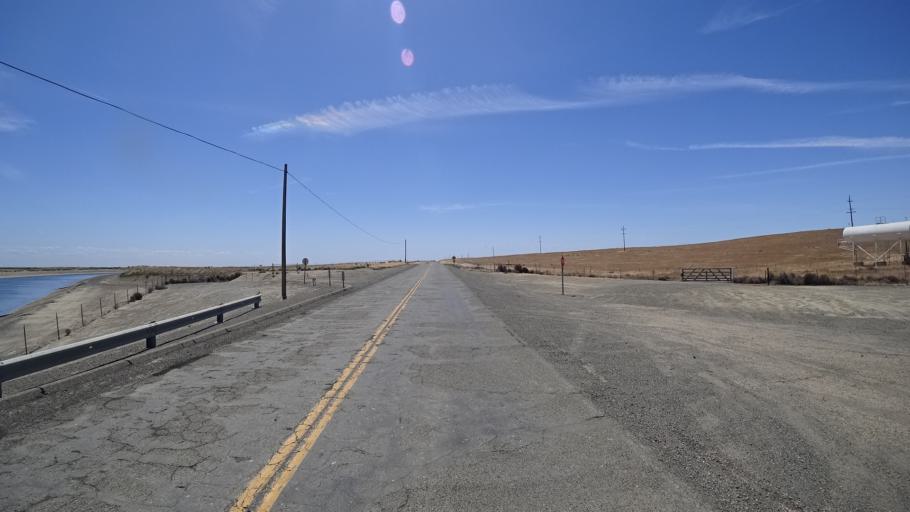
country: US
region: California
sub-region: Kings County
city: Kettleman City
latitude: 35.9059
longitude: -119.9150
